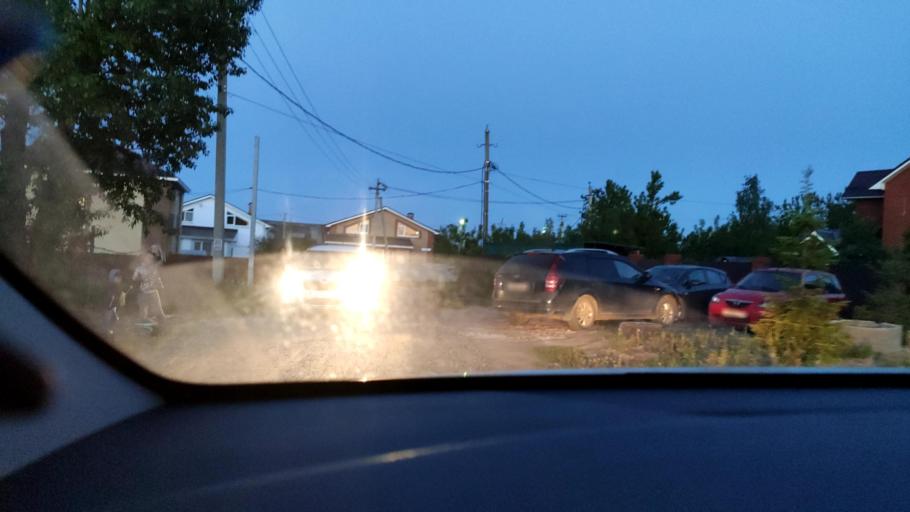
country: RU
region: Tatarstan
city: Stolbishchi
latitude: 55.7387
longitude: 49.2979
